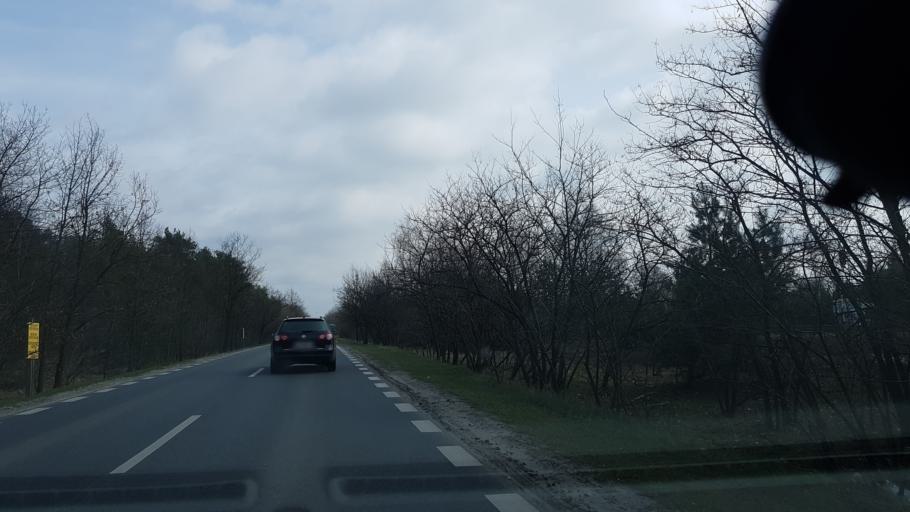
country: PL
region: Masovian Voivodeship
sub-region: Warszawa
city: Wesola
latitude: 52.2549
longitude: 21.2167
